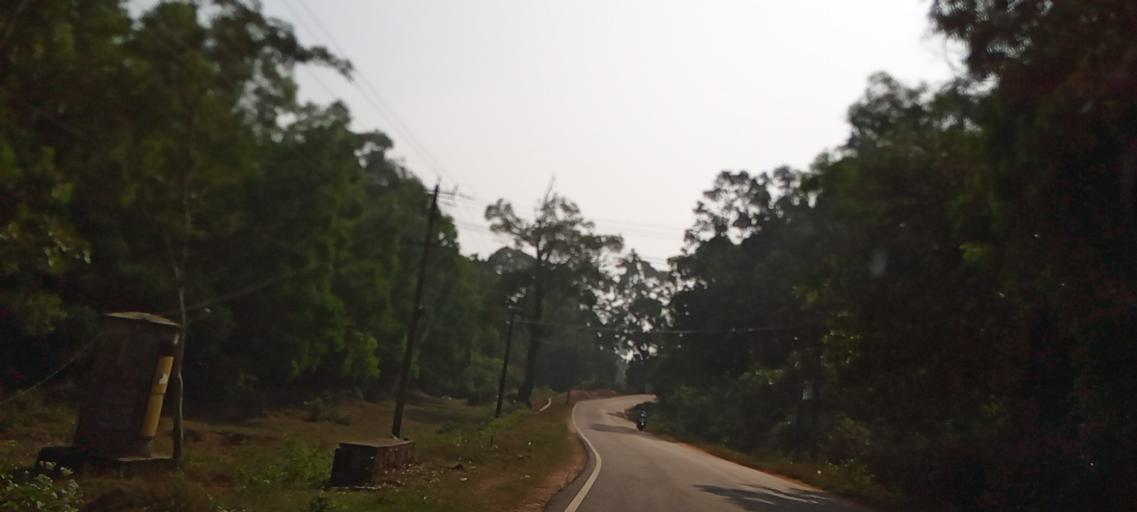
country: IN
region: Karnataka
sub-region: Udupi
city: Manipala
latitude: 13.5124
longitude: 74.8299
